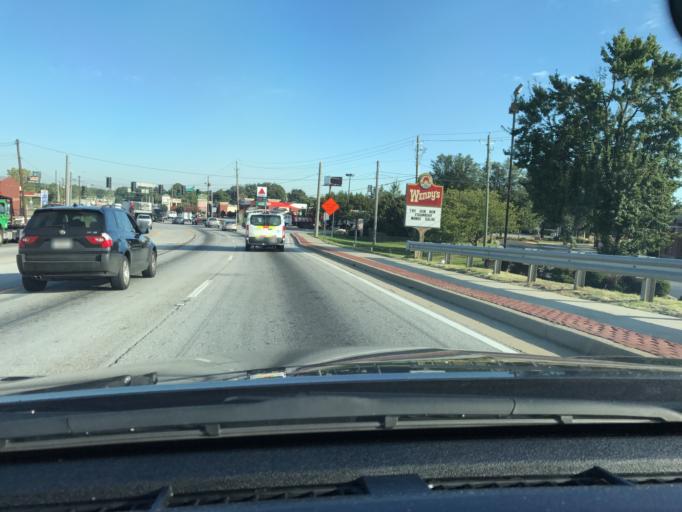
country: US
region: Georgia
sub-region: Clayton County
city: Forest Park
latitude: 33.6287
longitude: -84.3848
